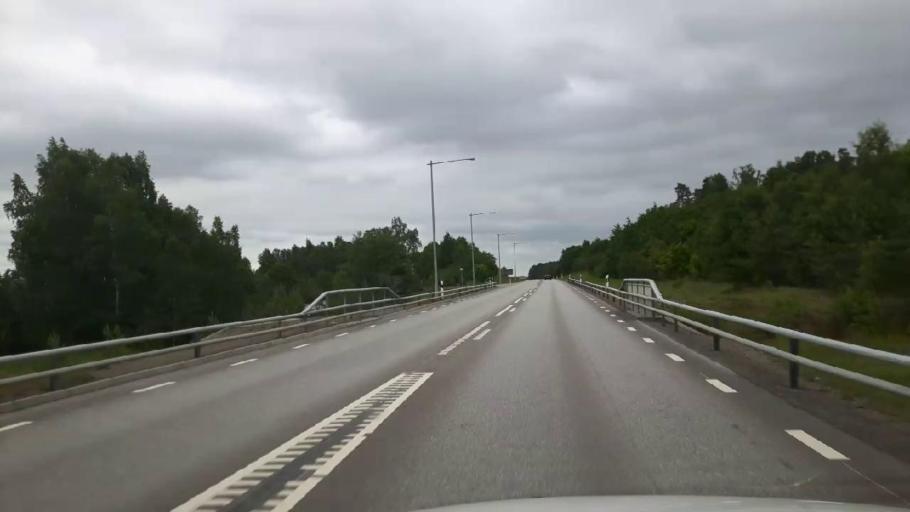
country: SE
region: Vaestmanland
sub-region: Kopings Kommun
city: Koping
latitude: 59.5432
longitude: 15.9327
